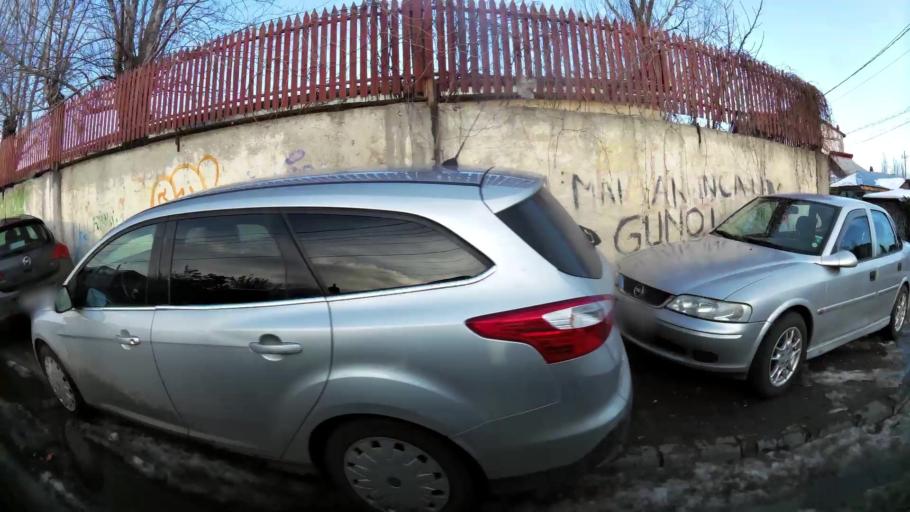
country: RO
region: Bucuresti
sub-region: Municipiul Bucuresti
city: Bucuresti
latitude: 44.3863
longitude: 26.0823
